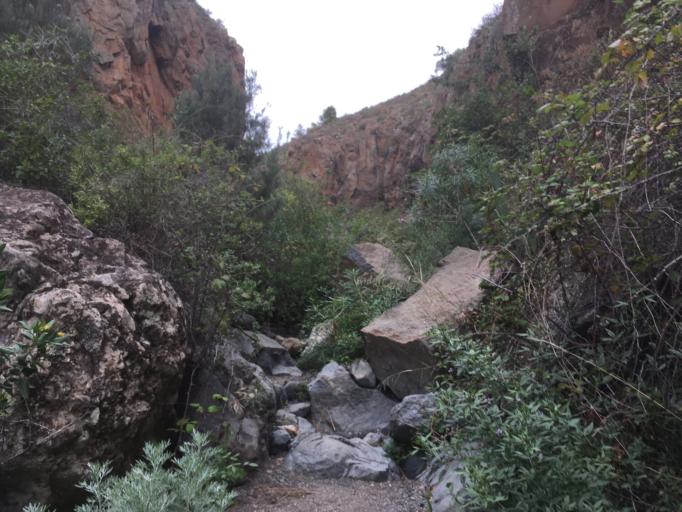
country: ES
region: Canary Islands
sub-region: Provincia de Santa Cruz de Tenerife
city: Lomo de Arico
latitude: 28.1805
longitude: -16.5132
